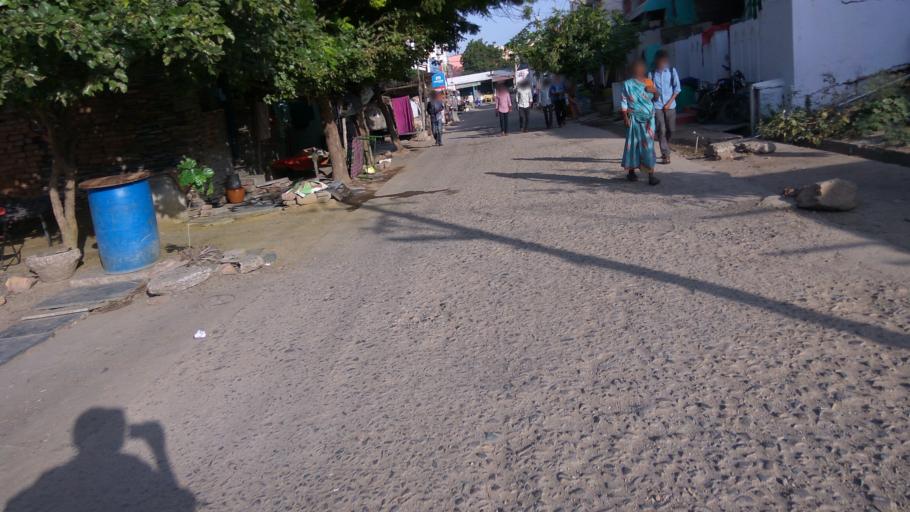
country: IN
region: Andhra Pradesh
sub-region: Prakasam
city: Markapur
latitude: 15.7439
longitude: 79.2740
